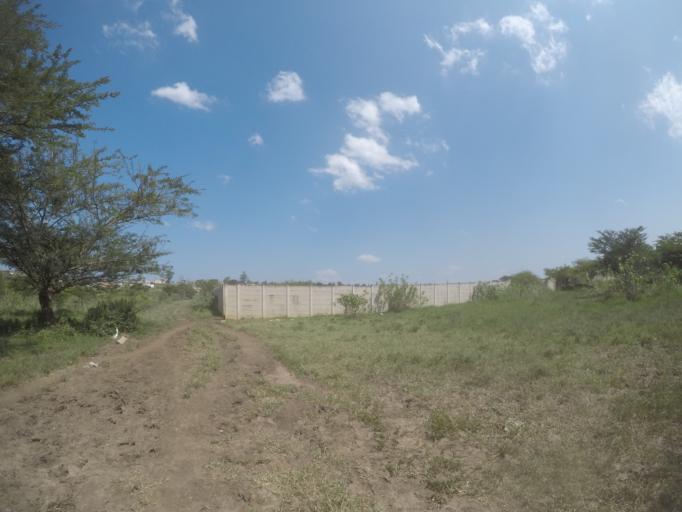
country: ZA
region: KwaZulu-Natal
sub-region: uThungulu District Municipality
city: Empangeni
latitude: -28.5859
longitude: 31.7421
